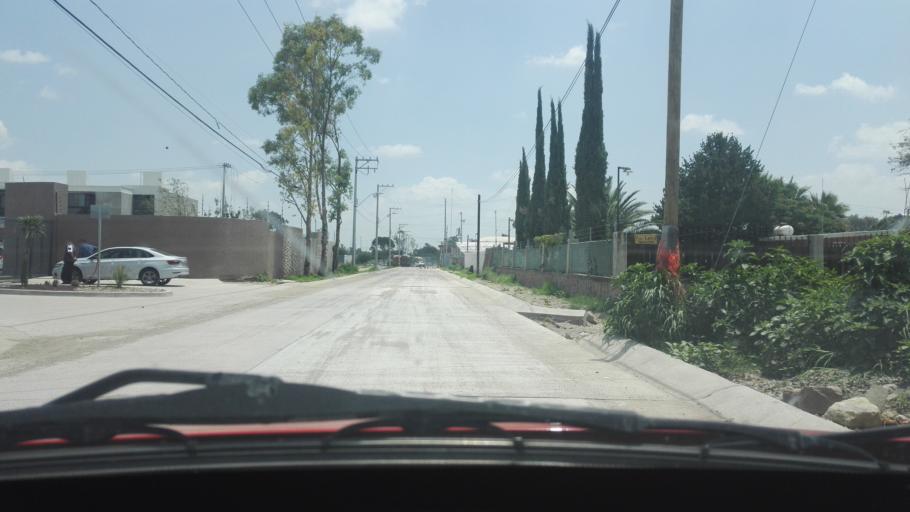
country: MX
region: Guanajuato
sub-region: Leon
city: Fraccionamiento Paraiso Real
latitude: 21.0741
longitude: -101.6099
